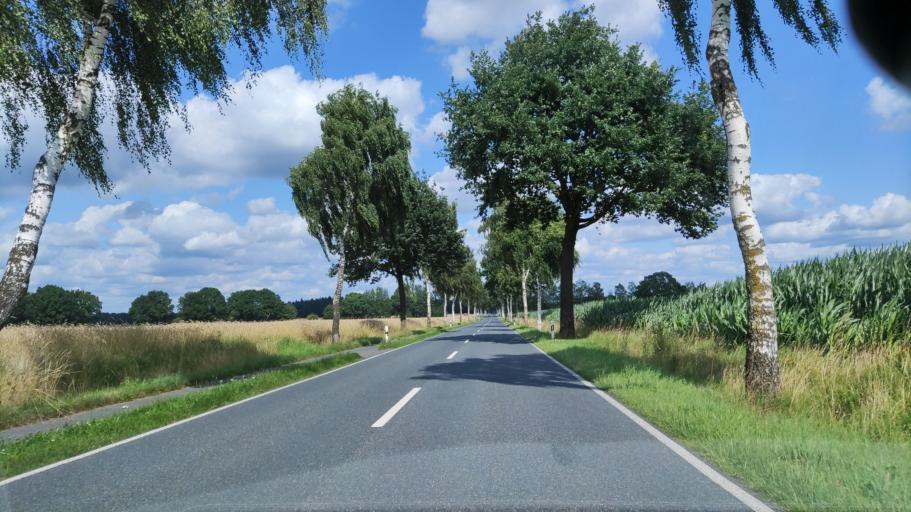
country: DE
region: Lower Saxony
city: Soltau
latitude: 52.9589
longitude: 9.7810
